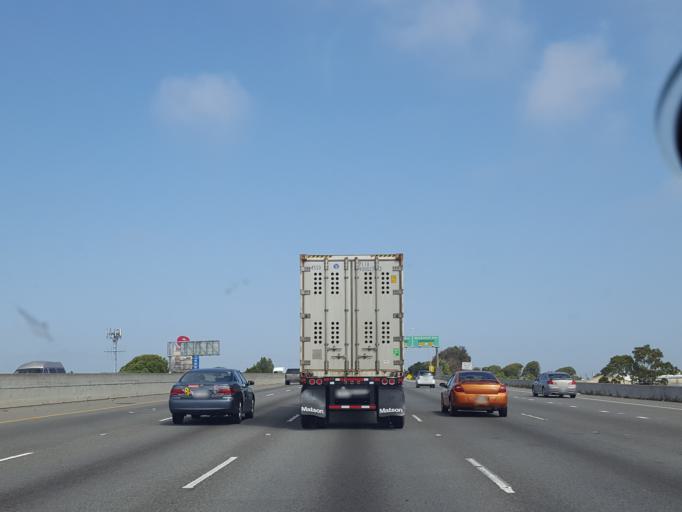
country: US
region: California
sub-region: Contra Costa County
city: East Richmond Heights
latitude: 37.9296
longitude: -122.3236
